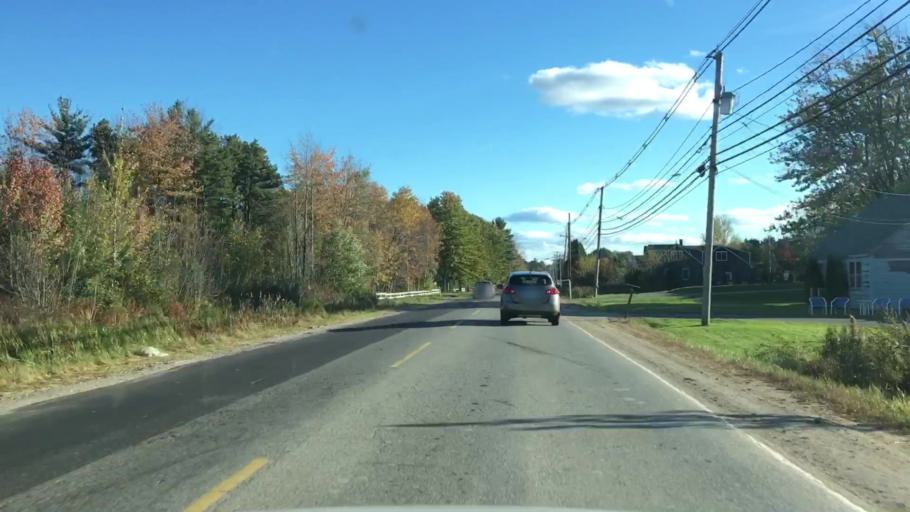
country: US
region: Maine
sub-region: Cumberland County
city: Scarborough
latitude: 43.6034
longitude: -70.3376
